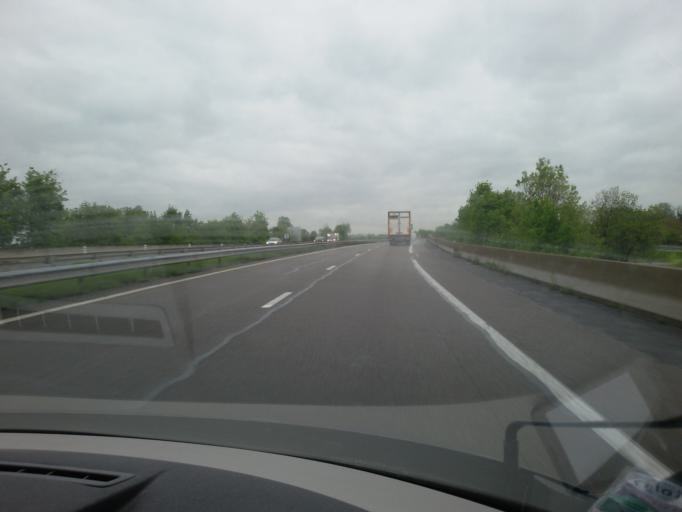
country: FR
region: Rhone-Alpes
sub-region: Departement du Rhone
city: Anse
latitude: 45.9262
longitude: 4.7261
